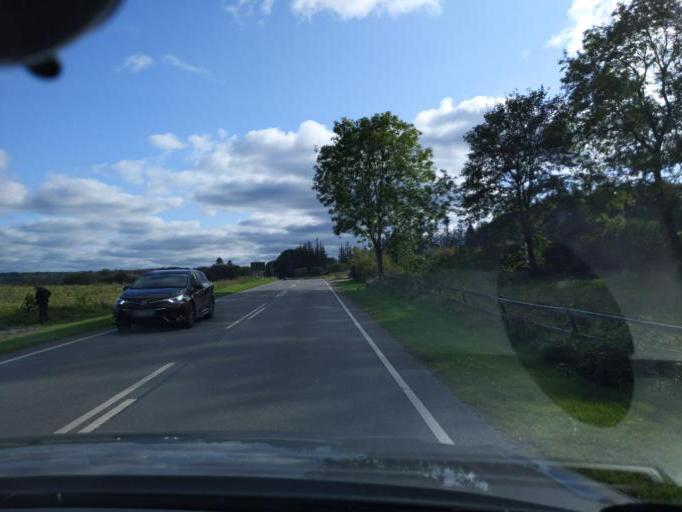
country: DK
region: North Denmark
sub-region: Mariagerfjord Kommune
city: Hobro
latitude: 56.5590
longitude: 9.7240
